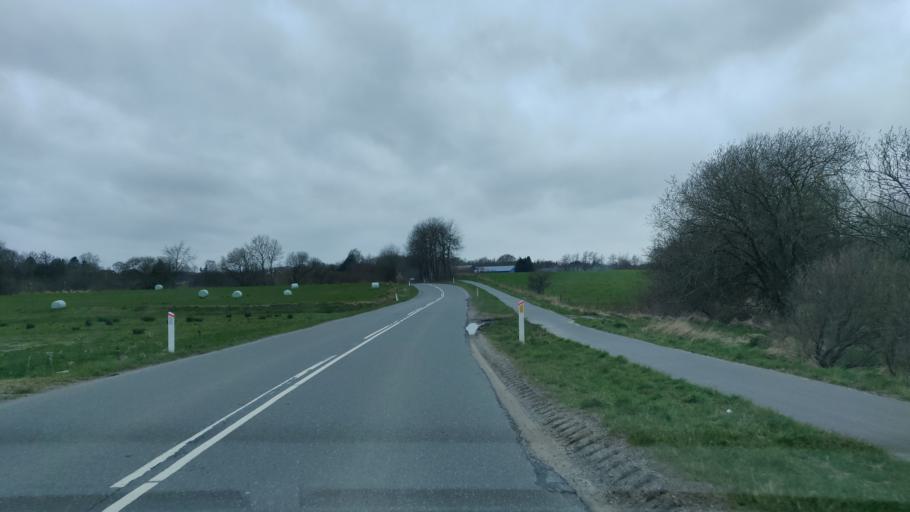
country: DK
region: Central Jutland
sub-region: Viborg Kommune
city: Stoholm
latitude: 56.4866
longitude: 9.1629
